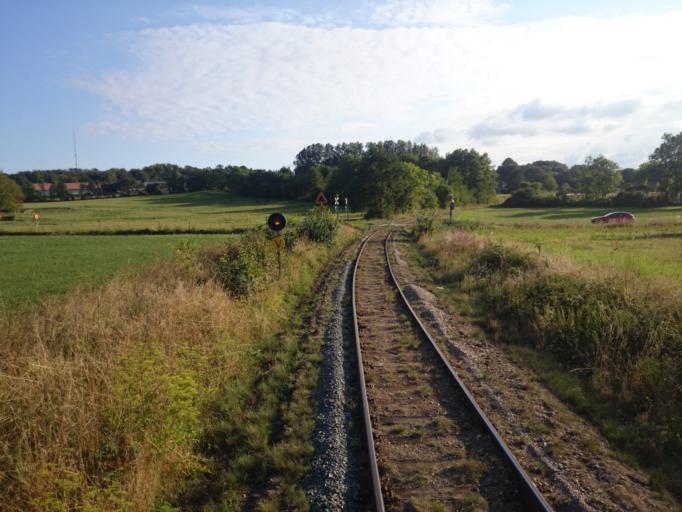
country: SE
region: Skane
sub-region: Simrishamns Kommun
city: Kivik
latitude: 55.6780
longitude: 14.1575
